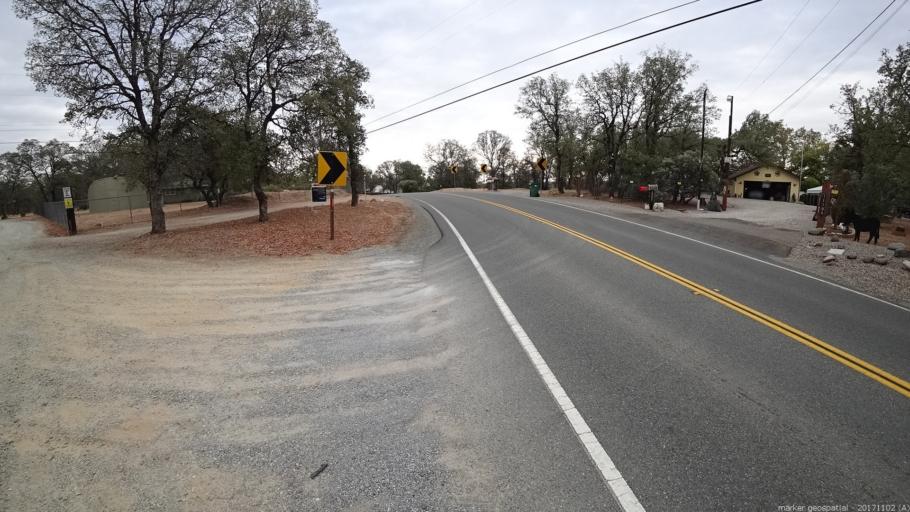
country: US
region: California
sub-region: Shasta County
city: Redding
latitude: 40.6151
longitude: -122.4214
